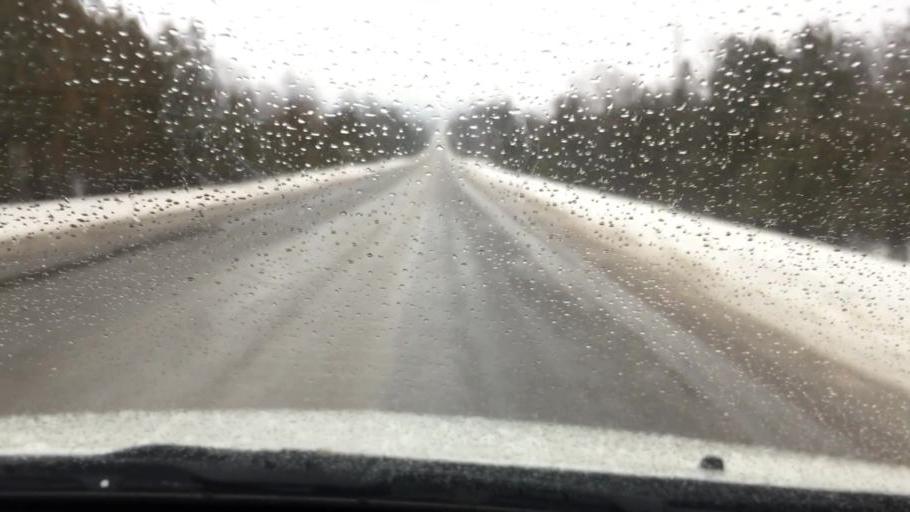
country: US
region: Michigan
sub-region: Charlevoix County
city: East Jordan
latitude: 45.1325
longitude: -85.1537
